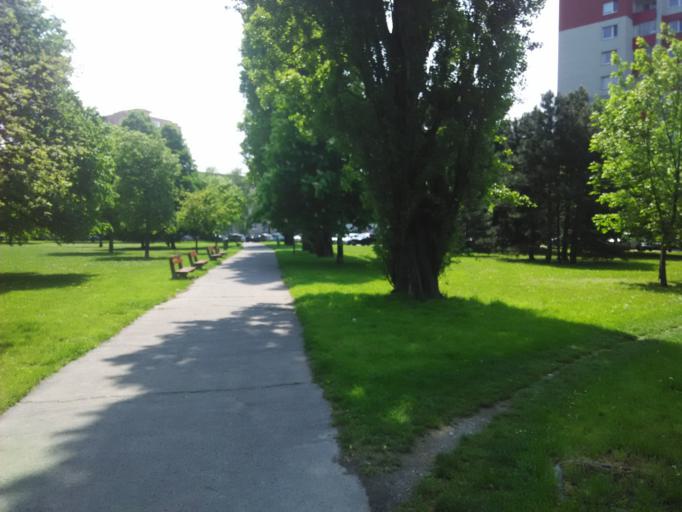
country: SK
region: Bratislavsky
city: Bratislava
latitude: 48.1626
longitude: 17.1487
